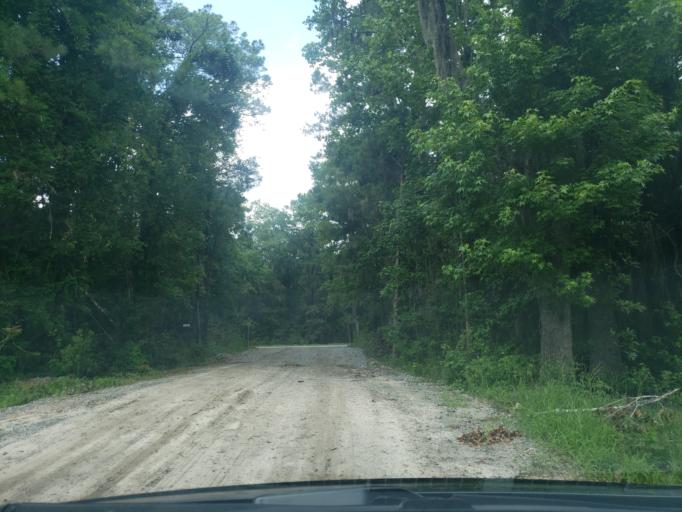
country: US
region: Georgia
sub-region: Bryan County
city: Richmond Hill
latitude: 32.0304
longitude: -81.3100
